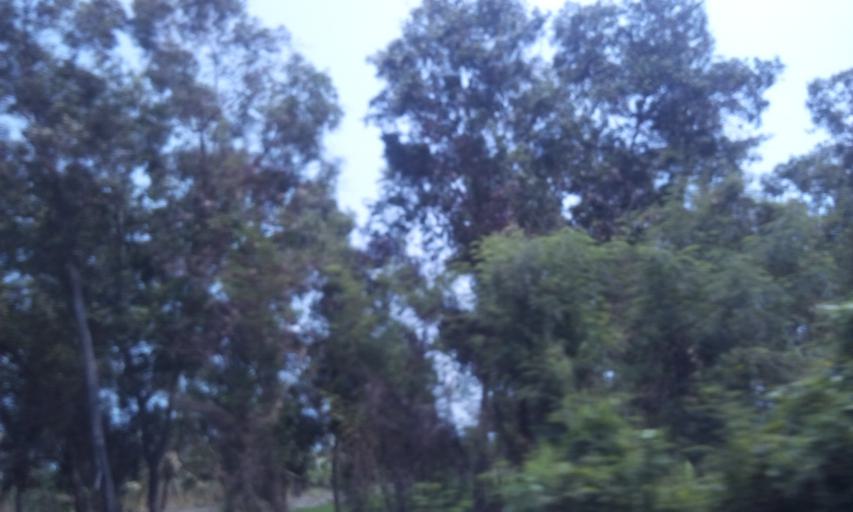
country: TH
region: Chachoengsao
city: Bang Nam Priao
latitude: 13.8516
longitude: 100.9653
